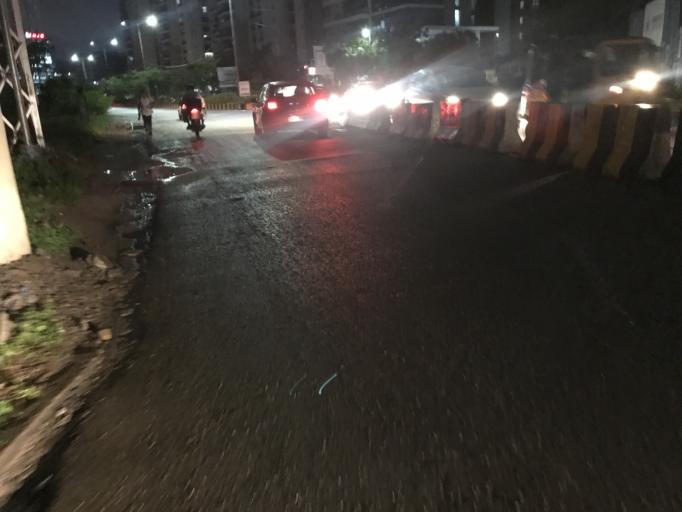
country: IN
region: Telangana
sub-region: Rangareddi
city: Kukatpalli
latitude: 17.4469
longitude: 78.3656
